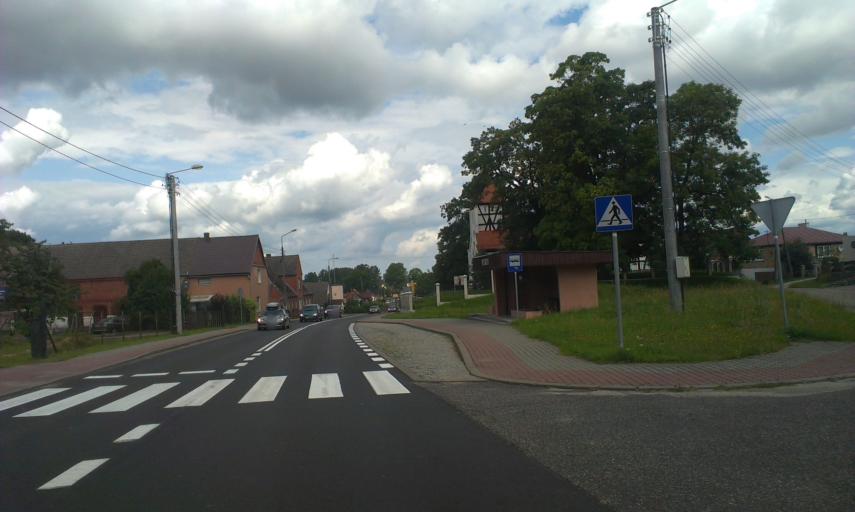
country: PL
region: West Pomeranian Voivodeship
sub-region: Powiat koszalinski
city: Bobolice
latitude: 54.0292
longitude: 16.4635
